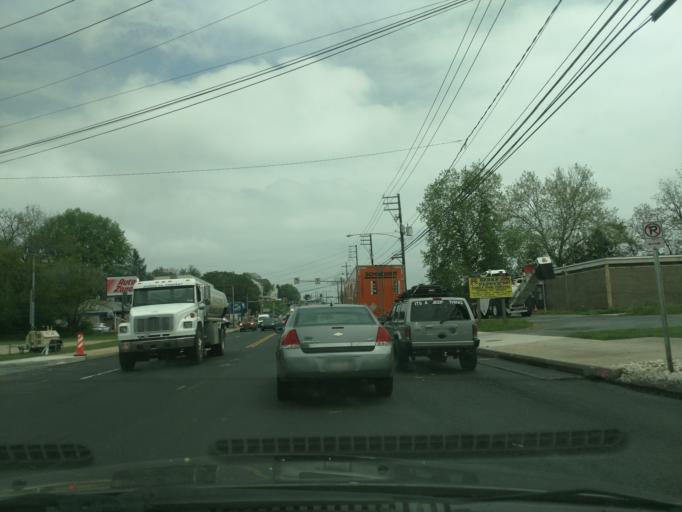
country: US
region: Pennsylvania
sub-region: Berks County
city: Sinking Spring
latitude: 40.3255
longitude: -76.0185
